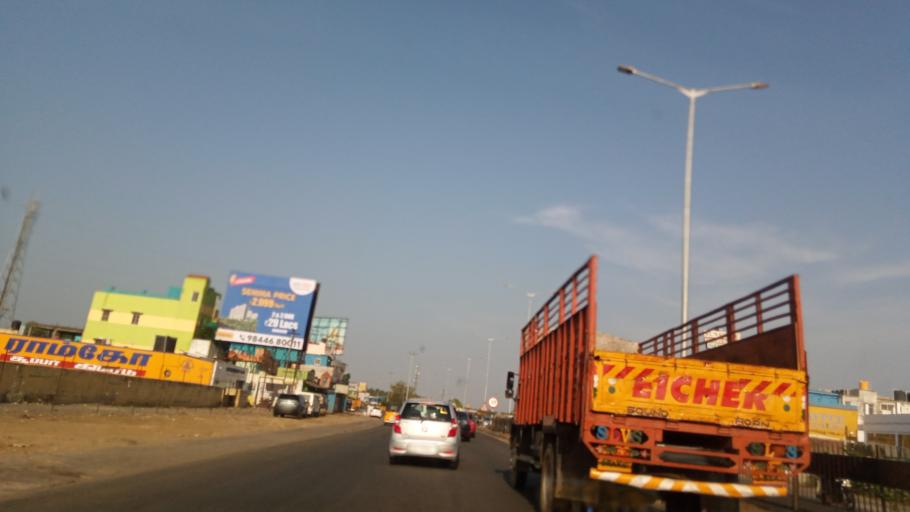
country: IN
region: Tamil Nadu
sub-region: Kancheepuram
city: Poonamalle
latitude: 13.0471
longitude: 80.0782
